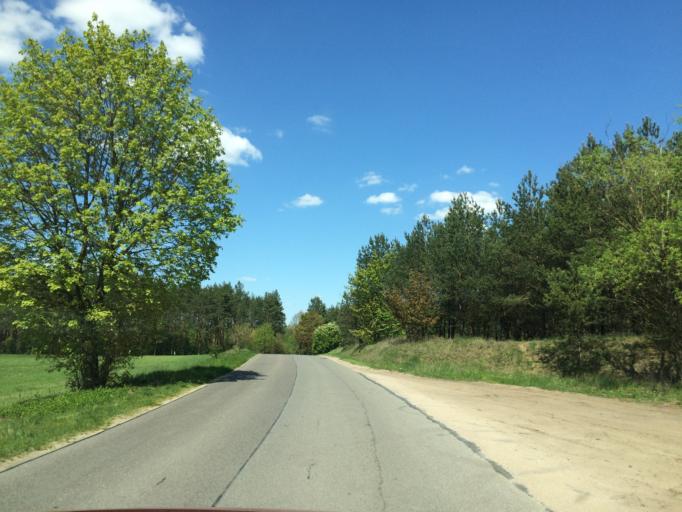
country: PL
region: Warmian-Masurian Voivodeship
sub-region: Powiat ilawski
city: Lubawa
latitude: 53.3915
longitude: 19.7361
